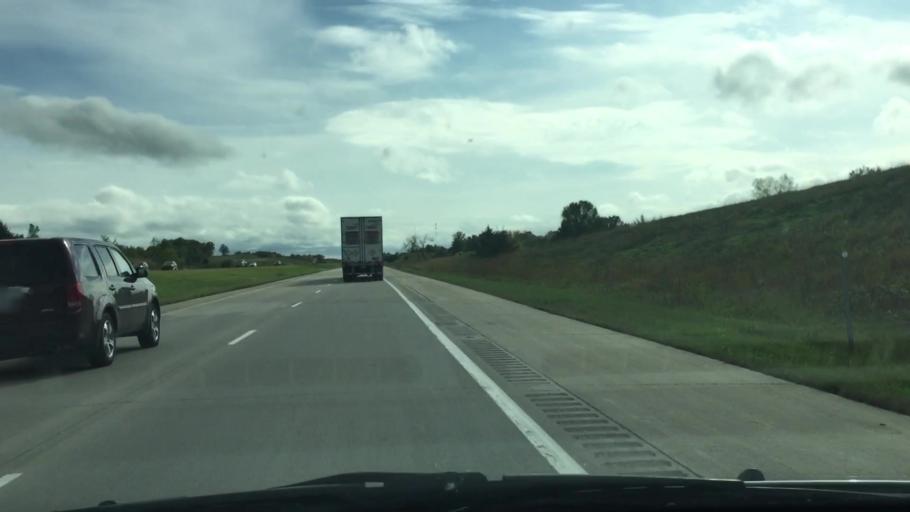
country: US
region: Iowa
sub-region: Clarke County
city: Osceola
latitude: 40.8868
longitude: -93.8012
